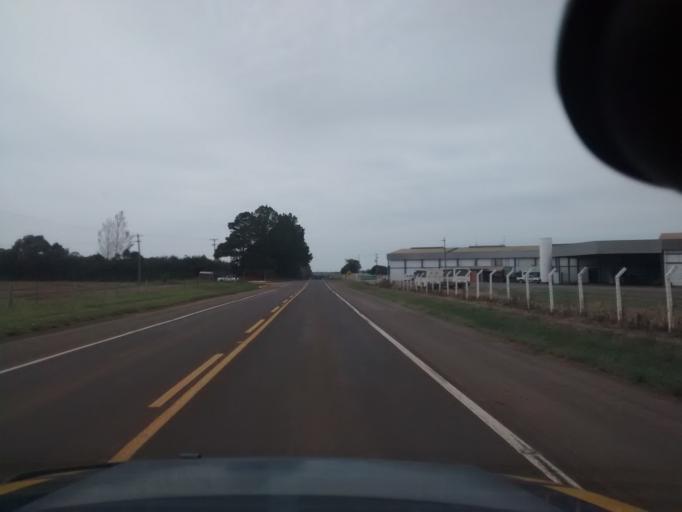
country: BR
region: Rio Grande do Sul
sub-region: Vacaria
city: Vacaria
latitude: -28.4352
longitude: -51.0092
